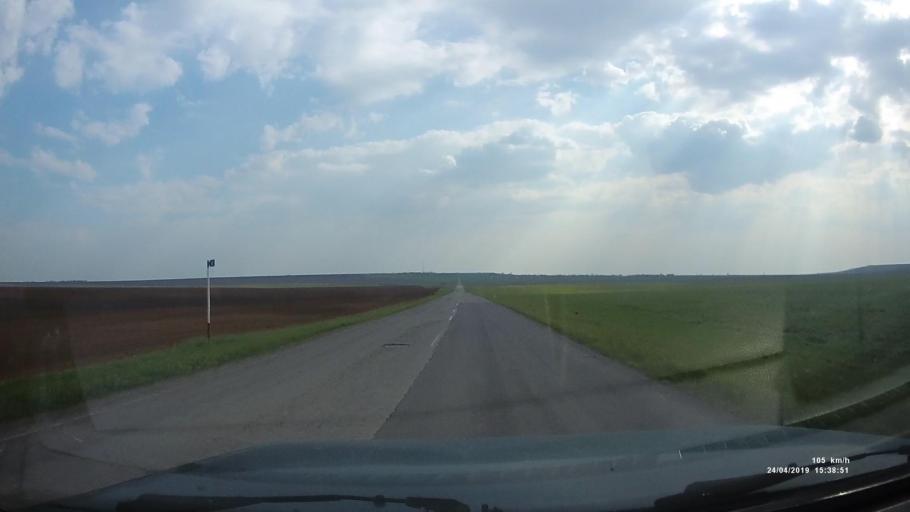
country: RU
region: Kalmykiya
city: Yashalta
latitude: 46.5928
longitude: 42.8224
